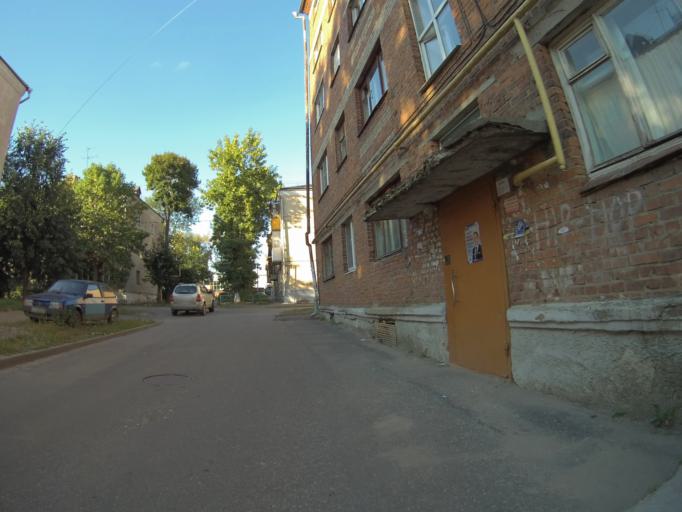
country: RU
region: Vladimir
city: Vladimir
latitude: 56.1459
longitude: 40.3906
